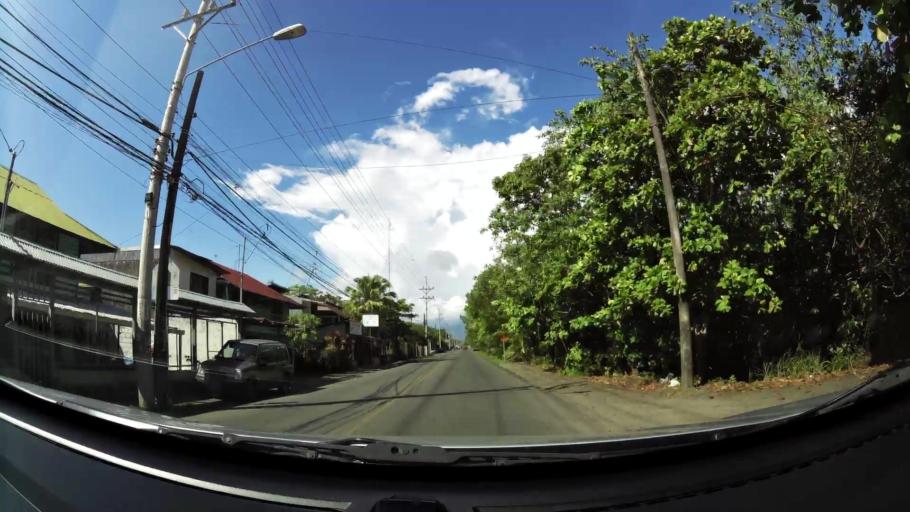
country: CR
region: Puntarenas
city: Quepos
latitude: 9.4375
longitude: -84.1643
